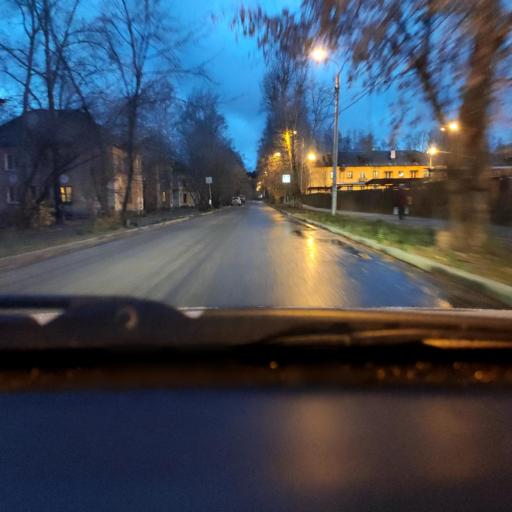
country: RU
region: Perm
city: Kondratovo
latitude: 58.0408
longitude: 56.1066
